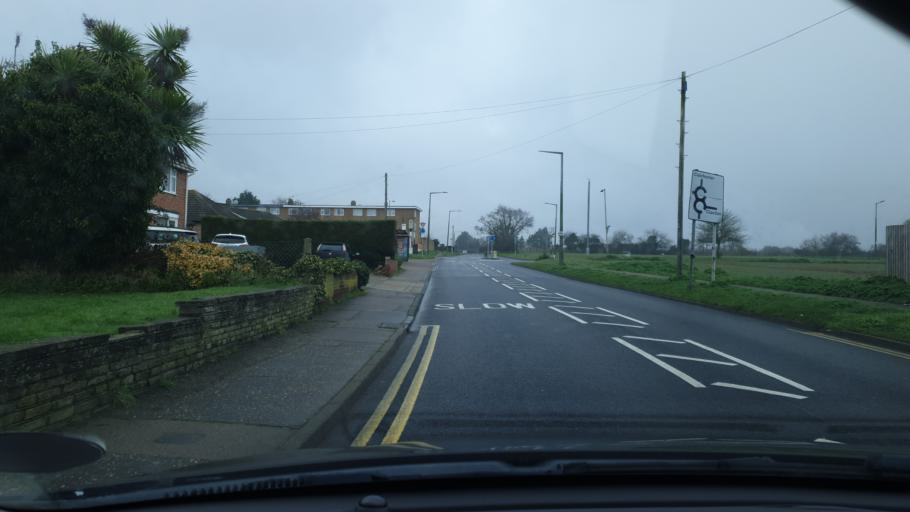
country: GB
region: England
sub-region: Essex
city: Clacton-on-Sea
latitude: 51.7817
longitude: 1.1203
